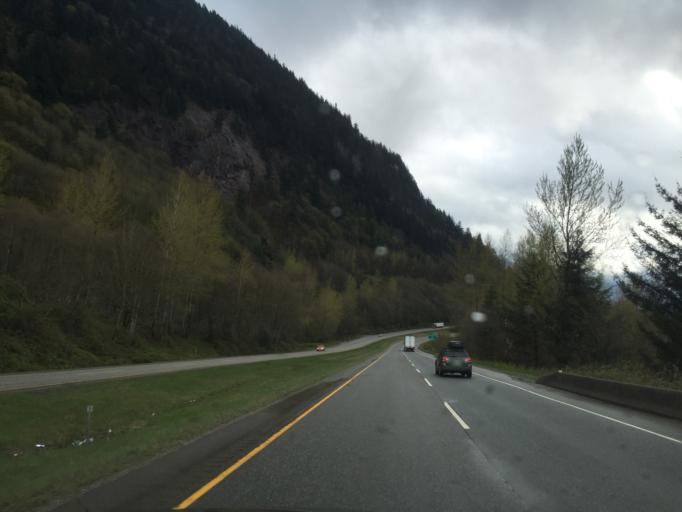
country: CA
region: British Columbia
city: Agassiz
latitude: 49.2797
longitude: -121.6716
